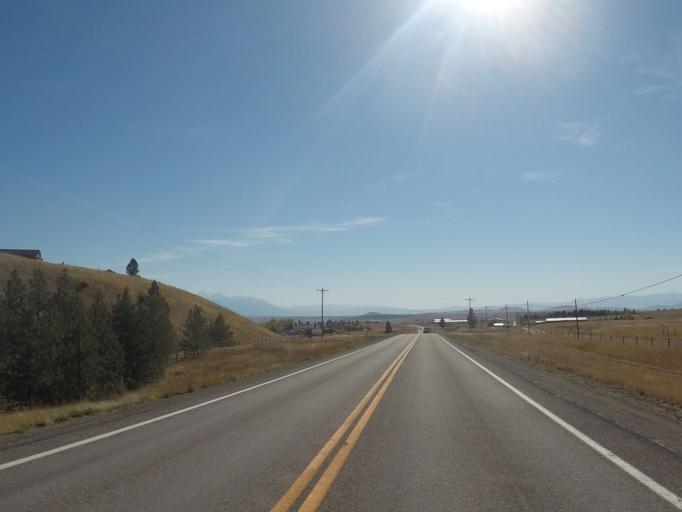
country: US
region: Montana
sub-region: Lake County
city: Polson
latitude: 47.7544
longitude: -114.2316
